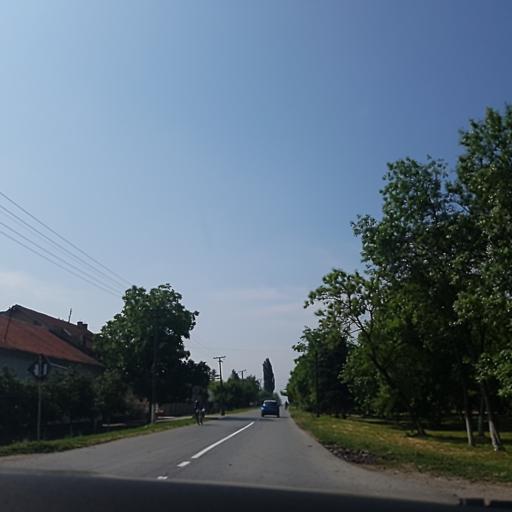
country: RS
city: Jarkovac
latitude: 45.2717
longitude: 20.7645
